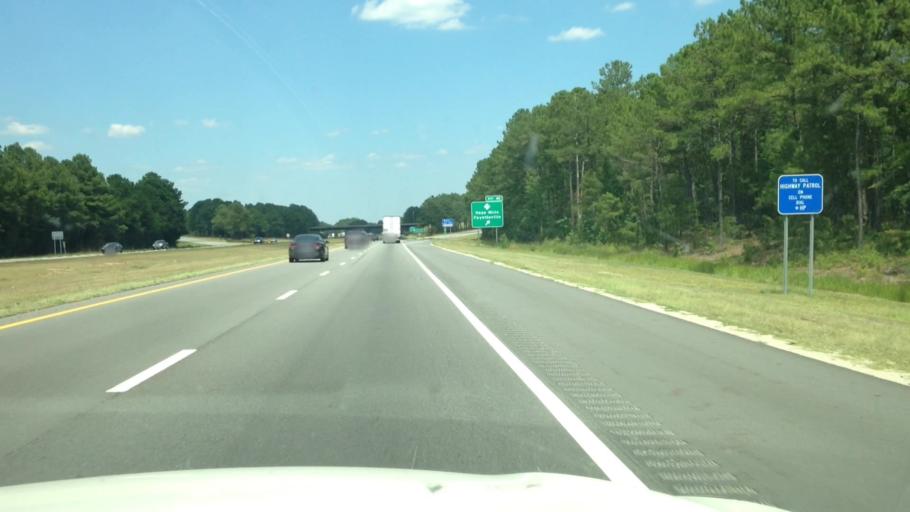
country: US
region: North Carolina
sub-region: Cumberland County
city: Hope Mills
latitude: 34.9357
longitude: -78.9285
